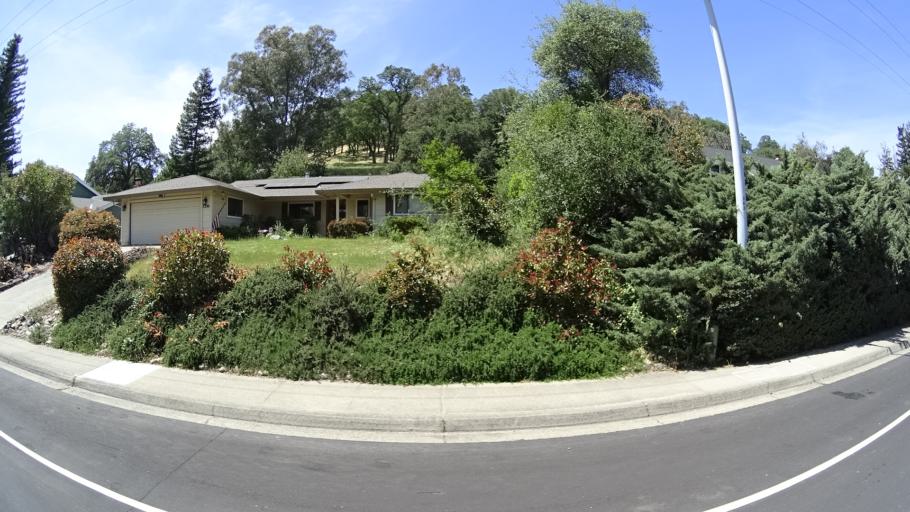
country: US
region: California
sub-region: Placer County
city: Rocklin
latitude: 38.7925
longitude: -121.2507
